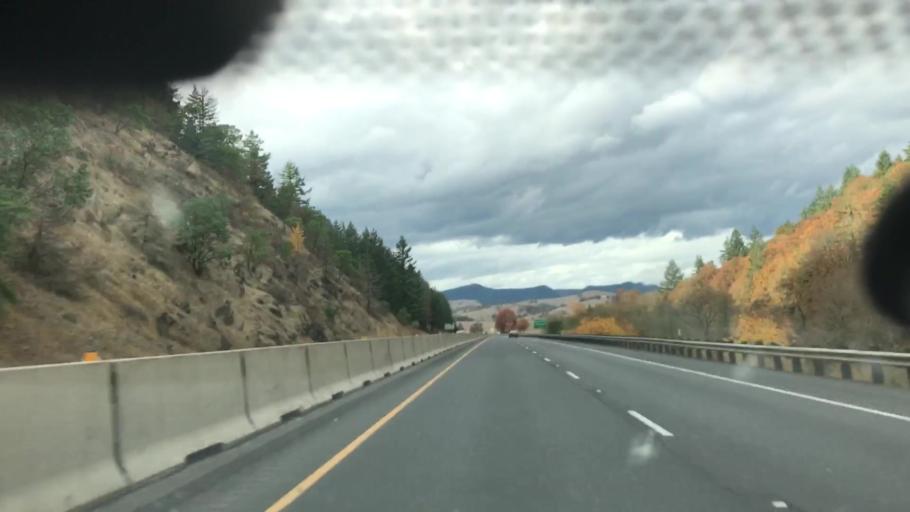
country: US
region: Oregon
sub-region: Douglas County
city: Sutherlin
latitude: 43.4431
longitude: -123.3191
